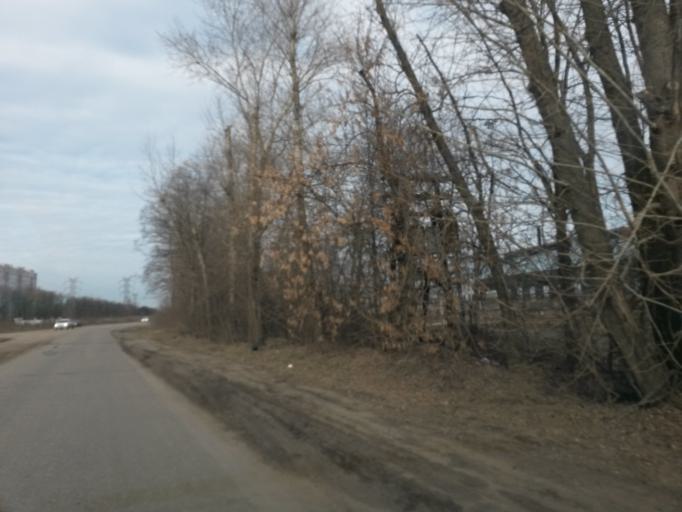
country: RU
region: Jaroslavl
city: Yaroslavl
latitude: 57.6437
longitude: 39.8490
